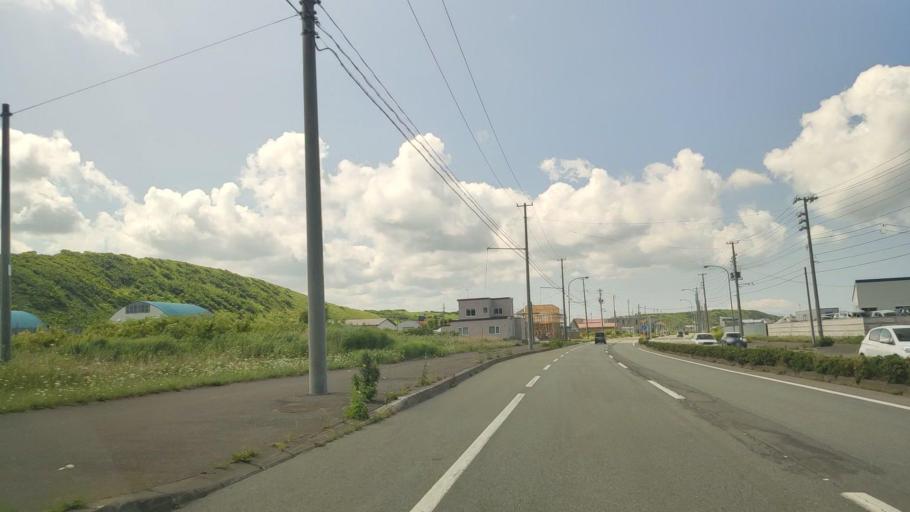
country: JP
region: Hokkaido
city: Wakkanai
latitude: 45.4015
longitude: 141.7434
